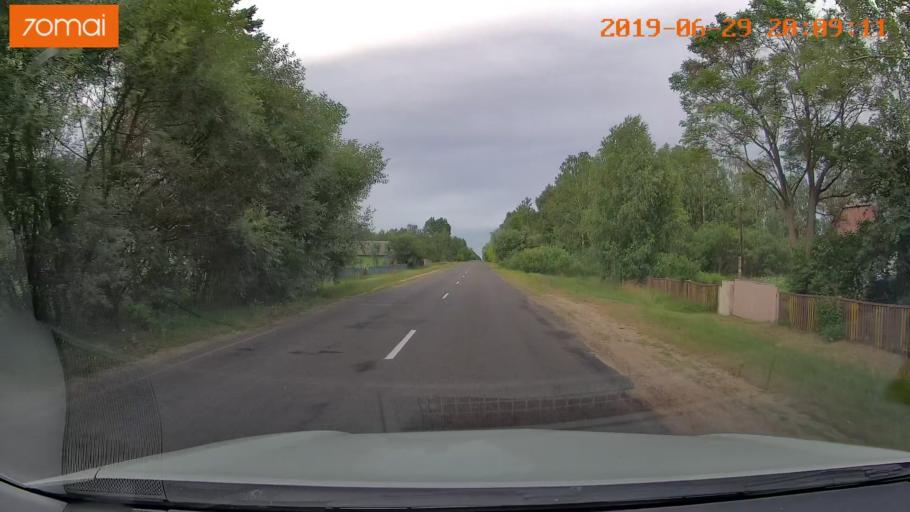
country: BY
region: Brest
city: Lahishyn
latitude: 52.3475
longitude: 26.0684
